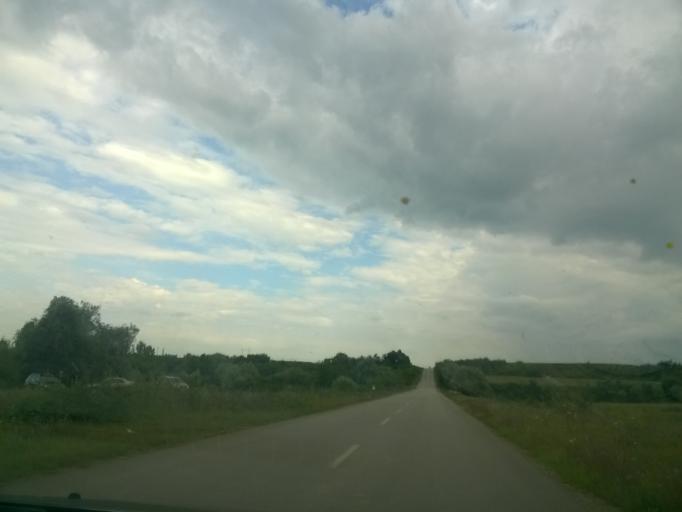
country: RS
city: Tomasevac
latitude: 45.2864
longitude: 20.6322
